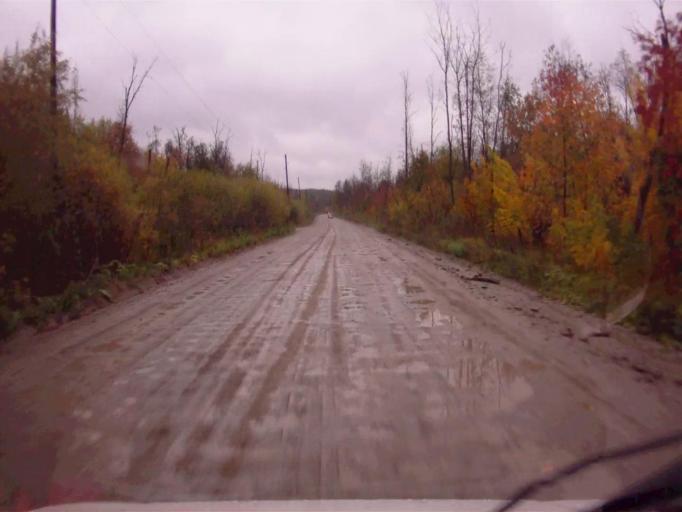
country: RU
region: Chelyabinsk
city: Kyshtym
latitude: 55.7351
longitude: 60.5156
